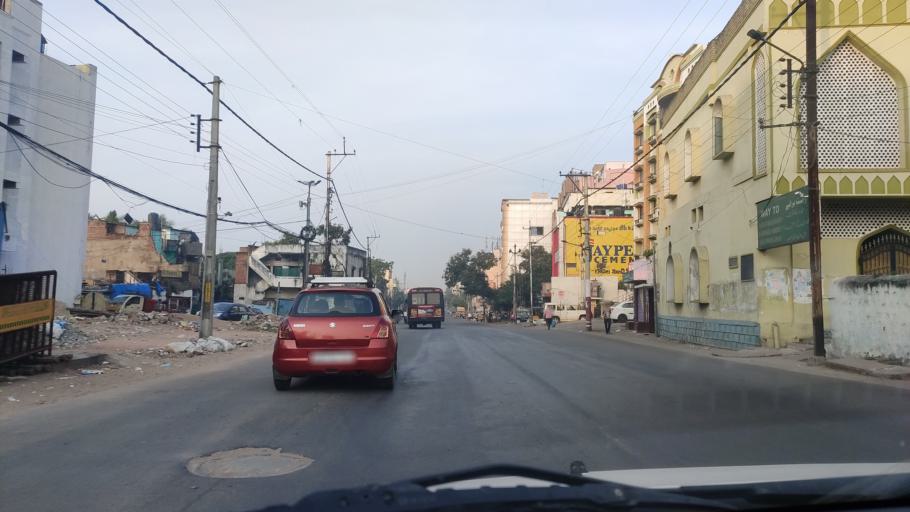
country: IN
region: Telangana
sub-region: Rangareddi
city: Gaddi Annaram
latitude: 17.3916
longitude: 78.5133
